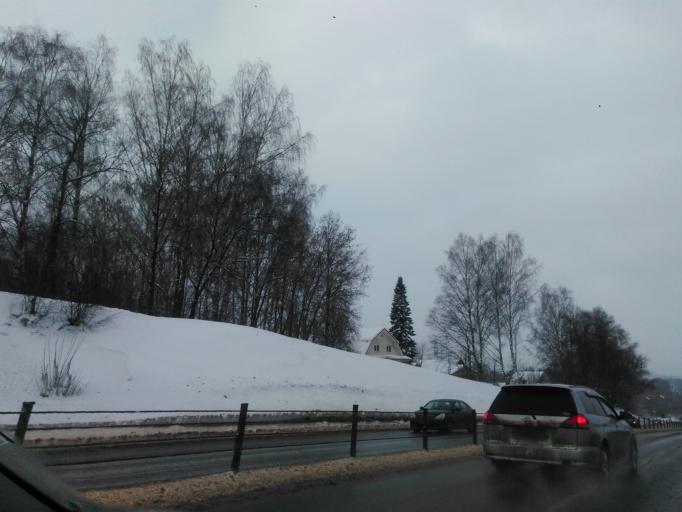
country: RU
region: Moskovskaya
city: Dedenevo
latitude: 56.2472
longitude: 37.5209
